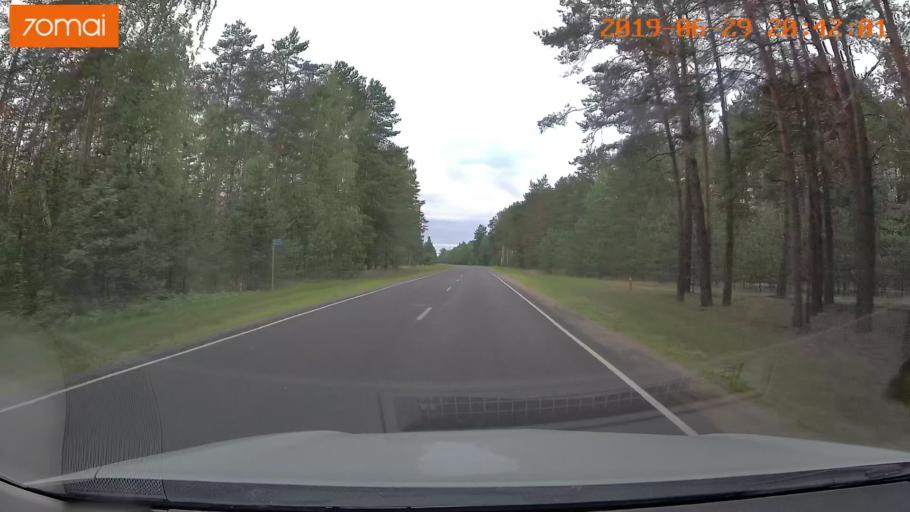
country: BY
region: Brest
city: Hantsavichy
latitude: 52.5927
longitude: 26.3319
